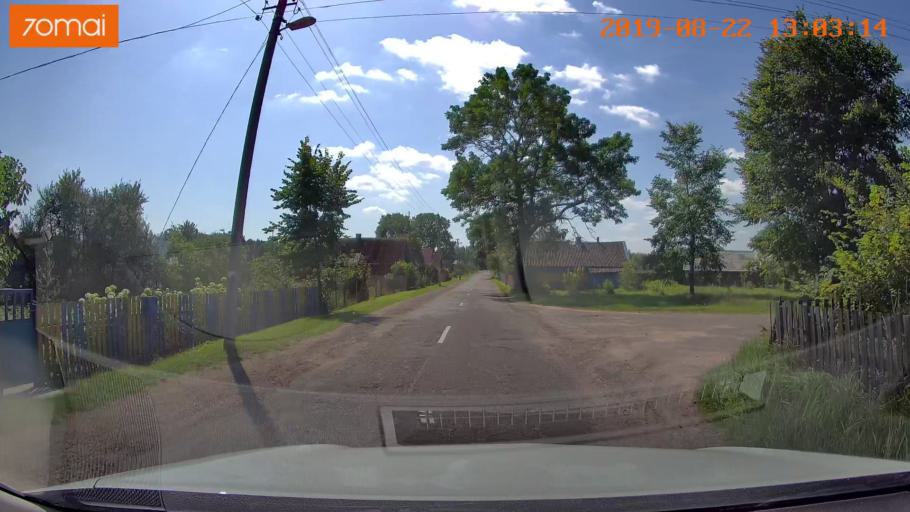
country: BY
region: Minsk
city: Prawdzinski
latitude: 53.3820
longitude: 27.8223
